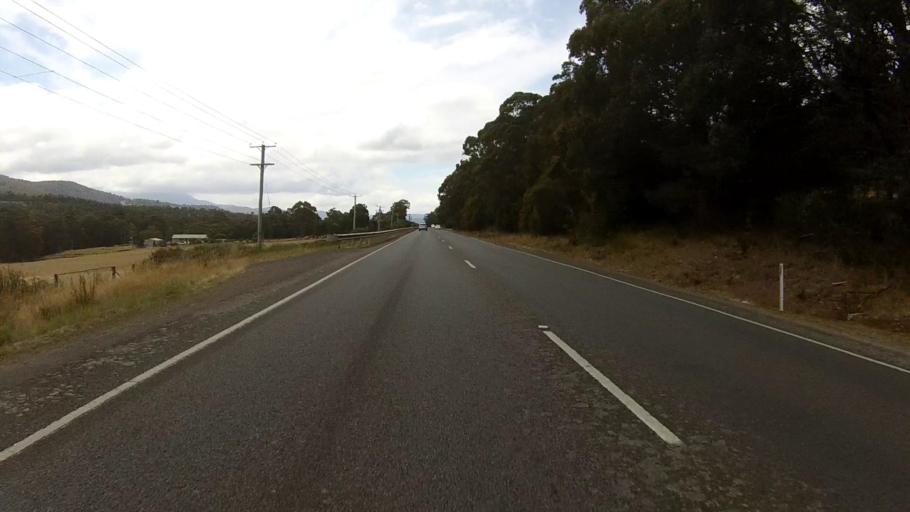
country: AU
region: Tasmania
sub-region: Kingborough
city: Kettering
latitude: -43.0840
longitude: 147.2529
